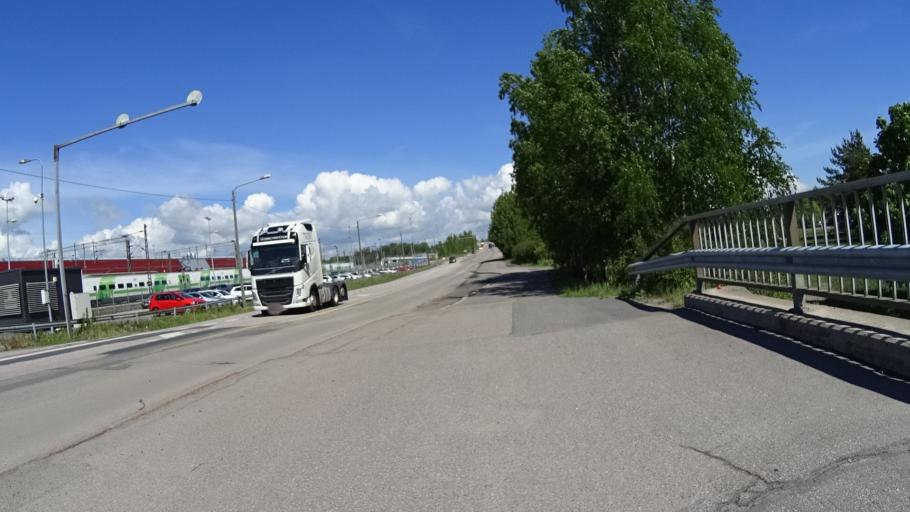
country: FI
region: Uusimaa
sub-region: Helsinki
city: Helsinki
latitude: 60.2121
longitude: 24.9317
